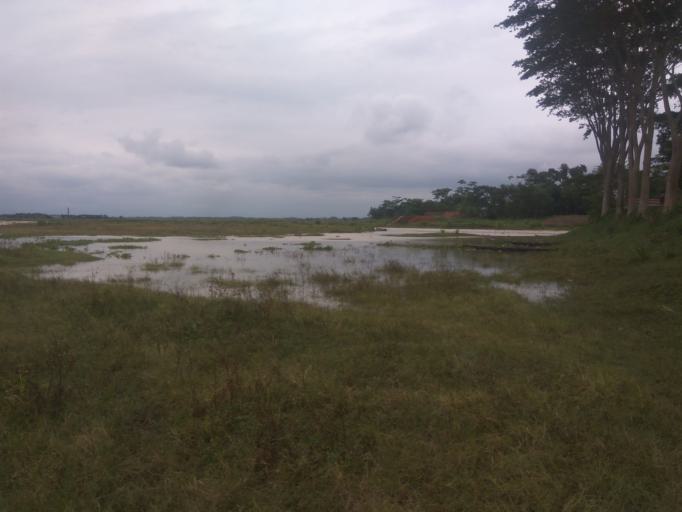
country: IN
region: Assam
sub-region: Karimganj
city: Karimganj
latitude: 24.8133
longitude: 92.2009
